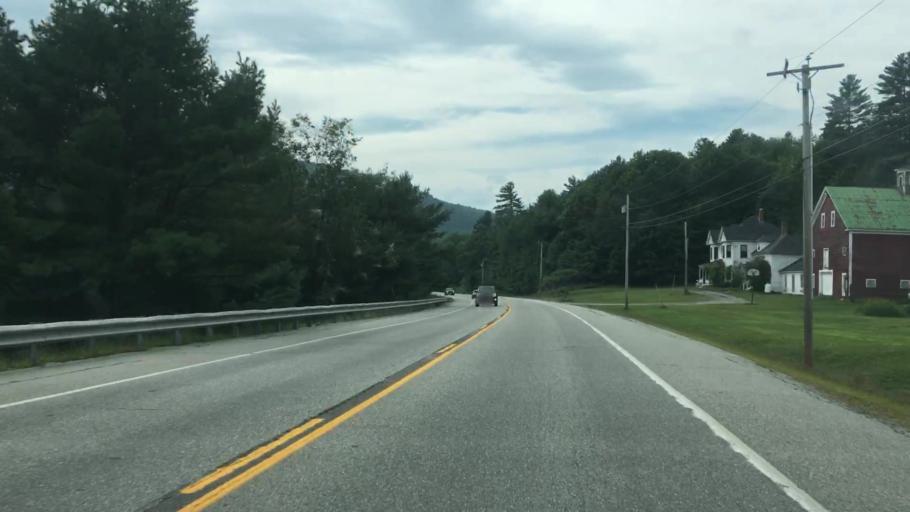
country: US
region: Maine
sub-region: Oxford County
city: Bethel
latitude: 44.4888
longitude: -70.7781
